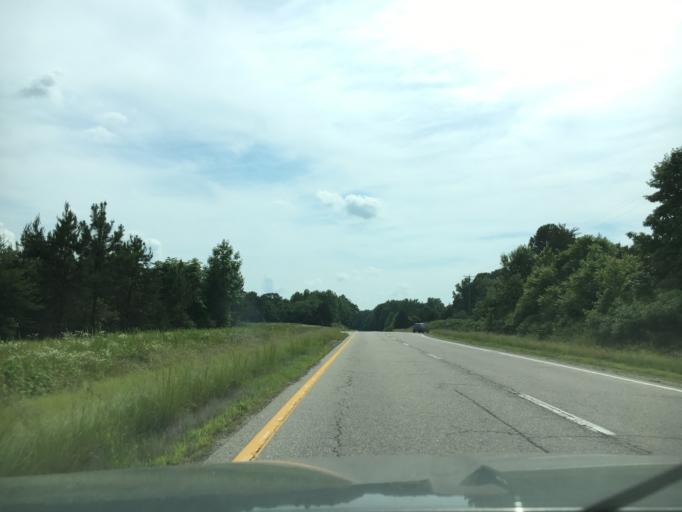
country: US
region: Virginia
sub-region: Lunenburg County
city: Victoria
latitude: 37.1440
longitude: -78.2996
